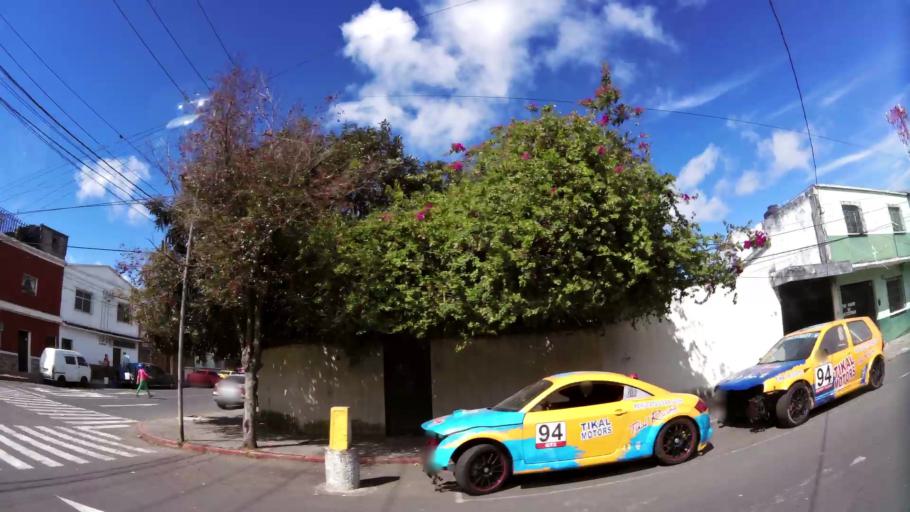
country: GT
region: Guatemala
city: Guatemala City
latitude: 14.6068
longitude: -90.5363
